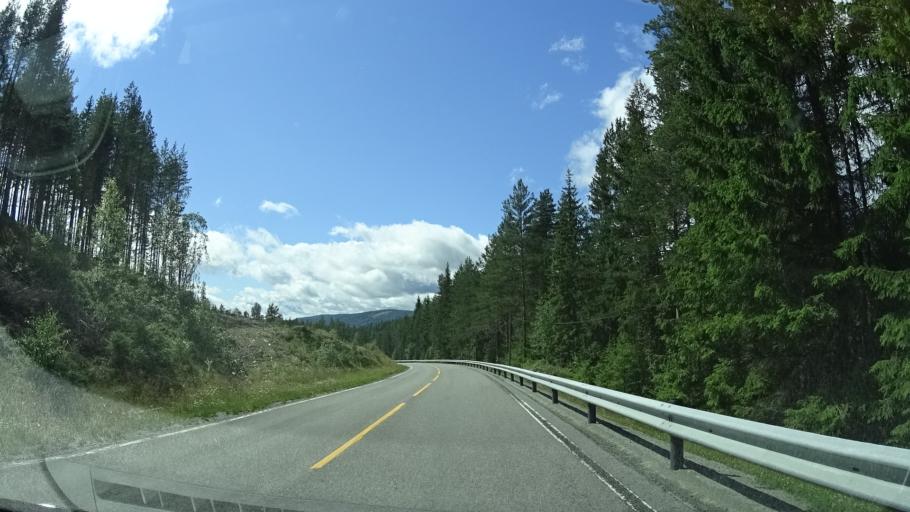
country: NO
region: Buskerud
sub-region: Krodsherad
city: Noresund
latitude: 60.1781
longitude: 9.7439
